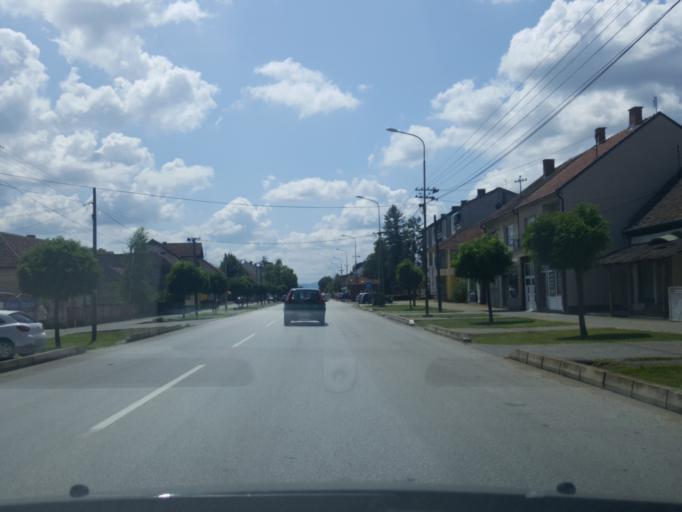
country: RS
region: Central Serbia
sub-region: Macvanski Okrug
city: Bogatic
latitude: 44.8388
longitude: 19.4804
